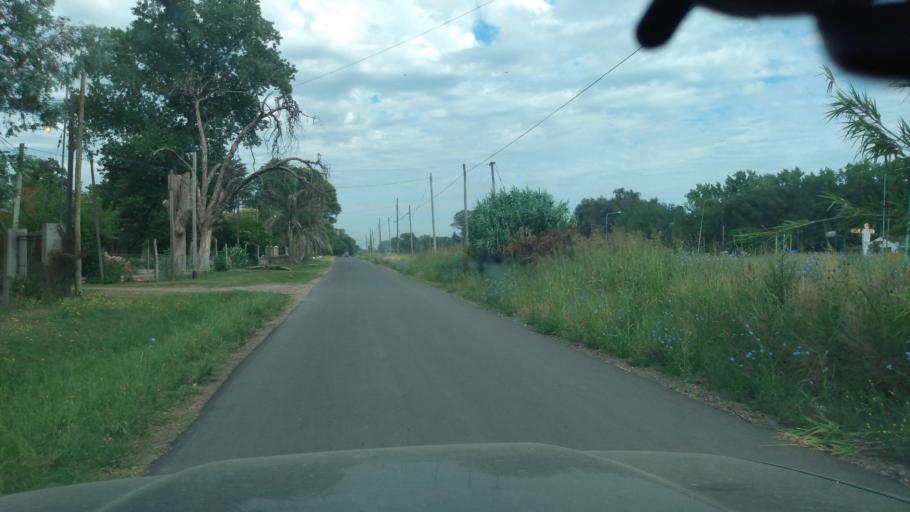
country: AR
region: Buenos Aires
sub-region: Partido de Lujan
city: Lujan
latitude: -34.5855
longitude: -59.0538
